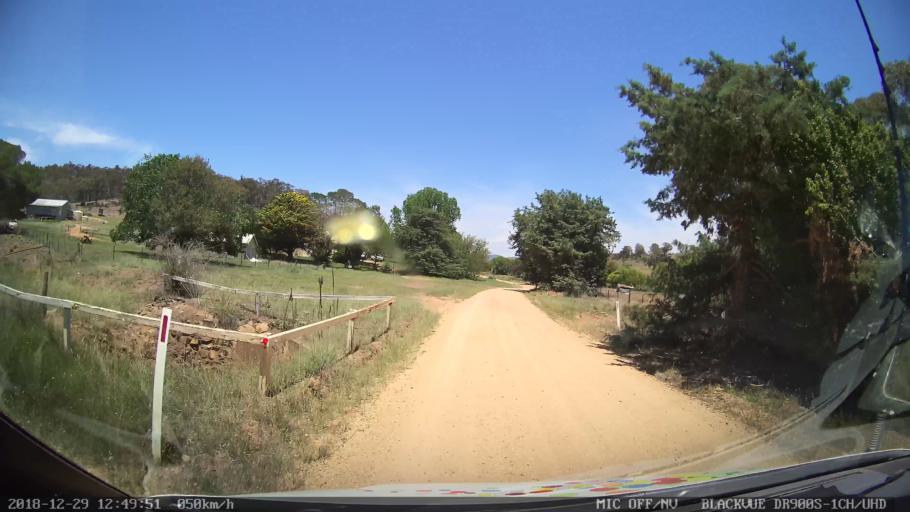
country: AU
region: Australian Capital Territory
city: Macarthur
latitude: -35.6668
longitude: 149.2051
